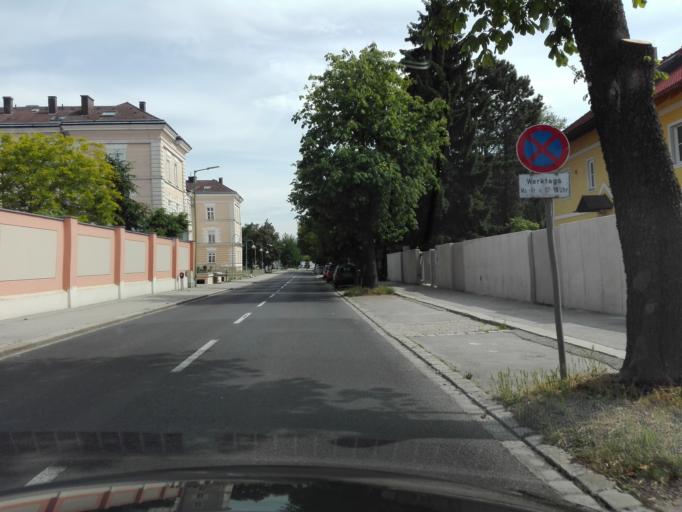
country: AT
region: Upper Austria
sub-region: Wels Stadt
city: Wels
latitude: 48.1655
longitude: 14.0319
